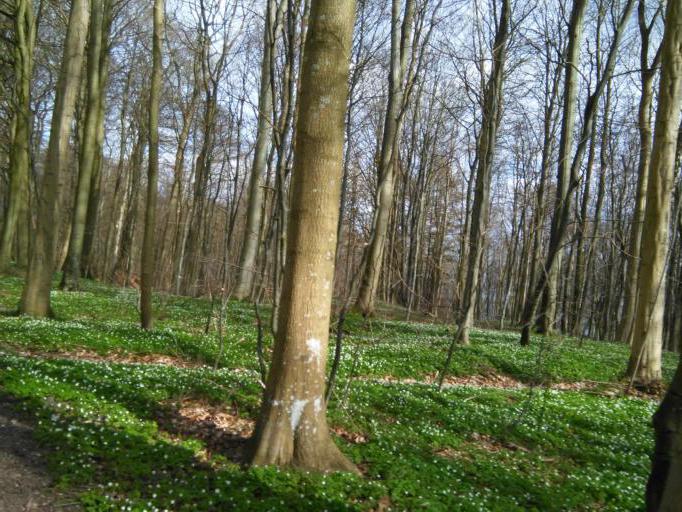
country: DK
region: Central Jutland
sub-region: Arhus Kommune
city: Beder
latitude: 56.0689
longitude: 10.2543
